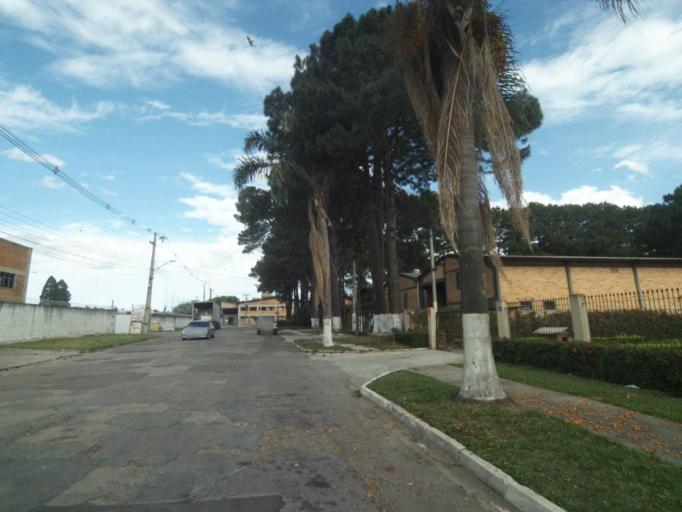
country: BR
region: Parana
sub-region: Curitiba
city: Curitiba
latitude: -25.4986
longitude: -49.3303
